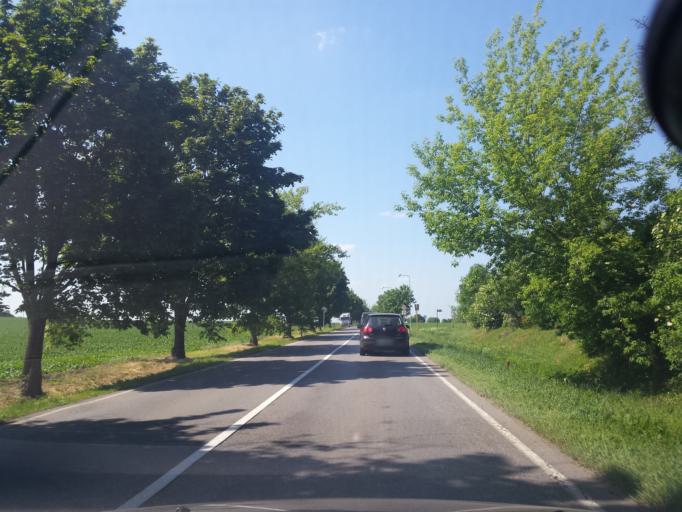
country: CZ
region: Central Bohemia
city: Velke Prilepy
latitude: 50.1936
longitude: 14.3202
